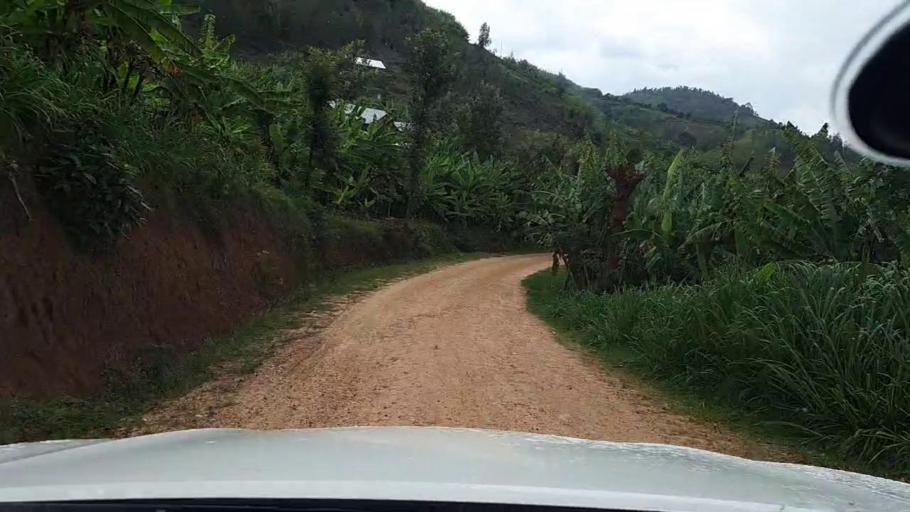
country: RW
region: Western Province
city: Kibuye
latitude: -2.1159
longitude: 29.4225
